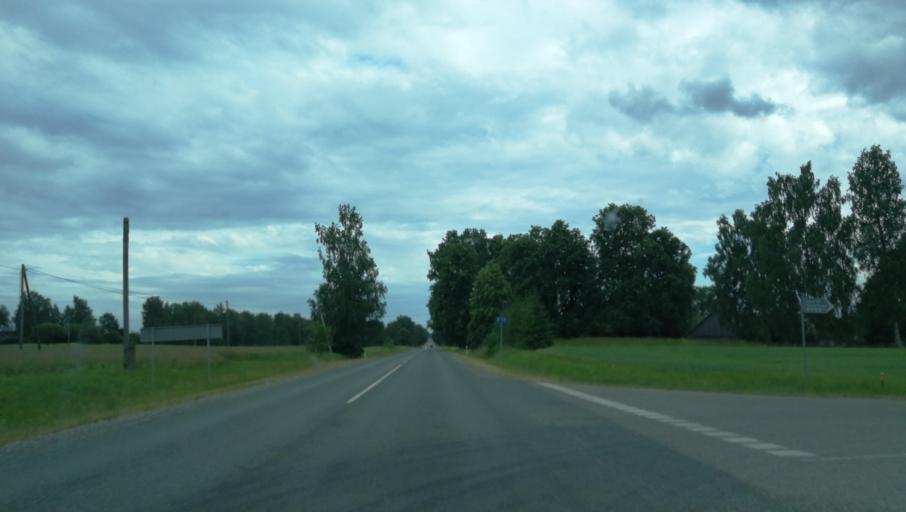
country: LV
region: Naukseni
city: Naukseni
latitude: 57.7194
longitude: 25.4234
